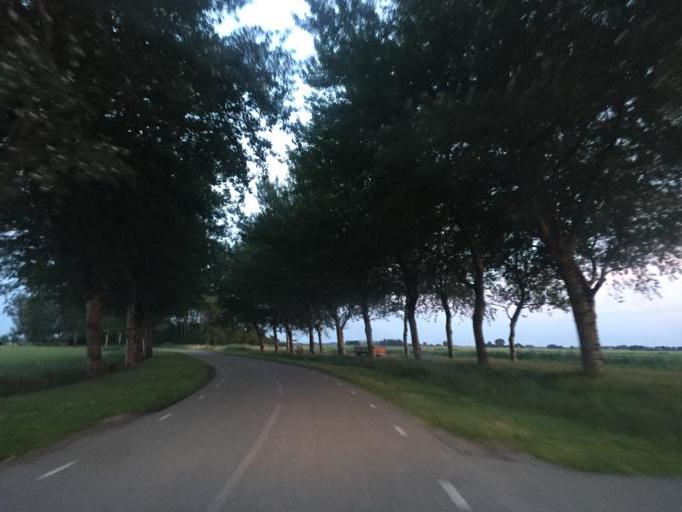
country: NL
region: Friesland
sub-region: Gemeente Dongeradeel
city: Anjum
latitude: 53.4001
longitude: 6.0857
